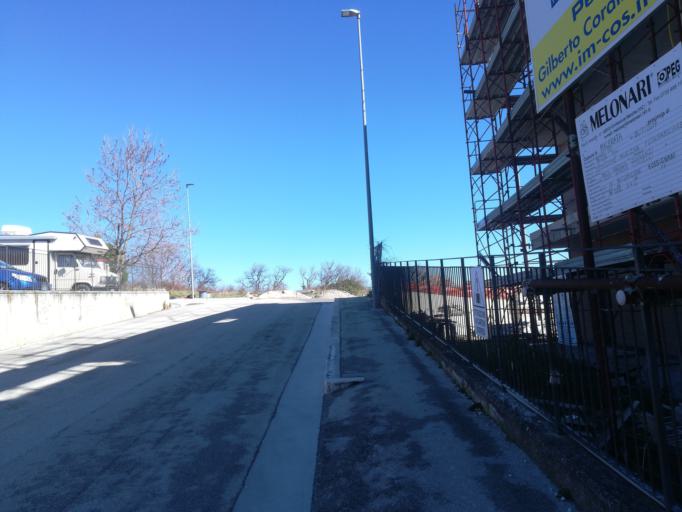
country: IT
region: The Marches
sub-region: Provincia di Macerata
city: Piediripa
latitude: 43.2895
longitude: 13.4758
